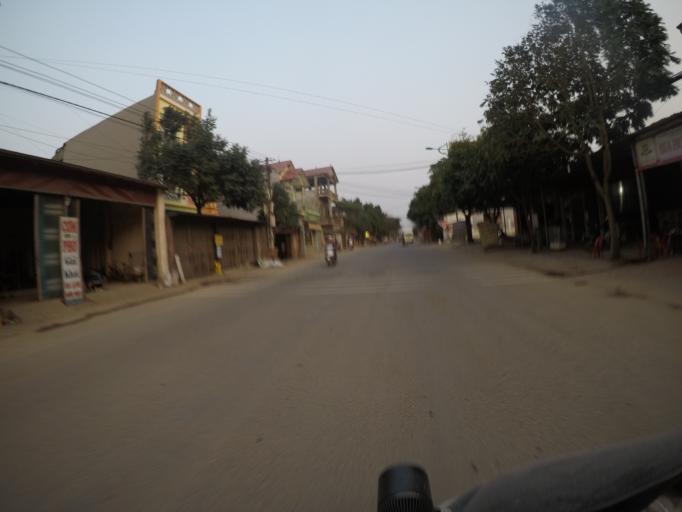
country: VN
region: Vinh Phuc
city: Trai Ngau
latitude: 21.4265
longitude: 105.5925
